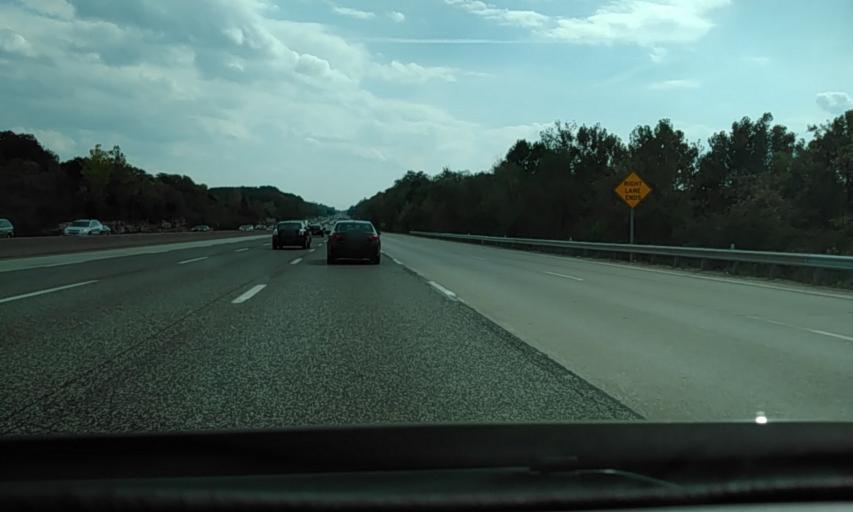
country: US
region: Missouri
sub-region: Saint Louis County
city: Sunset Hills
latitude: 38.5414
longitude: -90.4199
